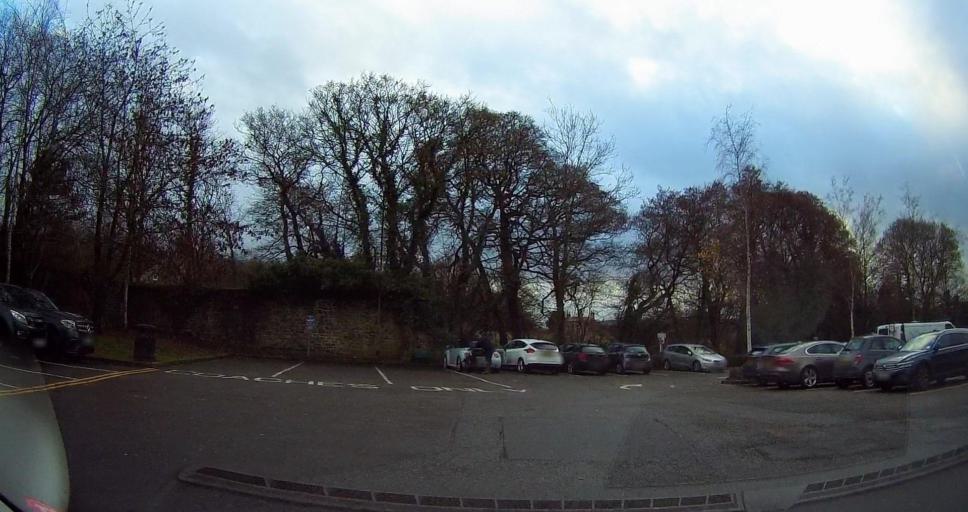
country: GB
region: England
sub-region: Derbyshire
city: Bakewell
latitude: 53.2455
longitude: -1.6143
